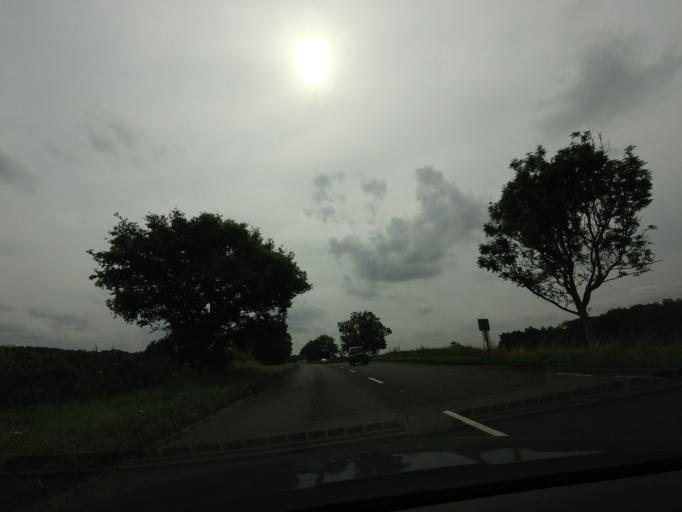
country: GB
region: England
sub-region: Shropshire
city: Tong
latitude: 52.6808
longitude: -2.3119
